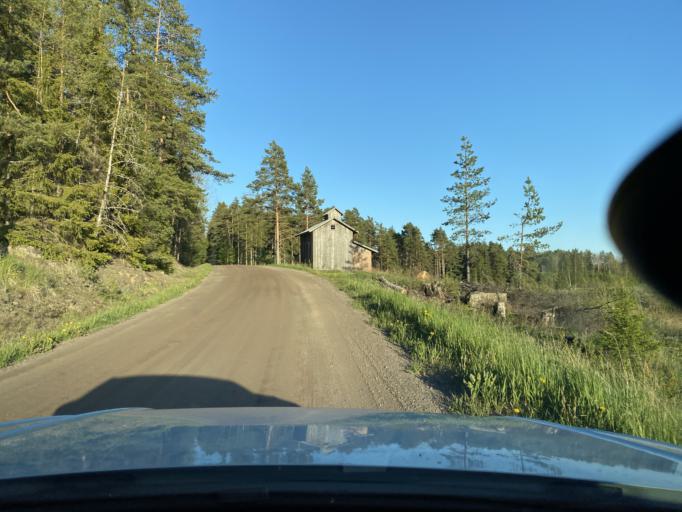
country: FI
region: Satakunta
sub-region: Rauma
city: Lappi
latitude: 61.1376
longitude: 21.9643
